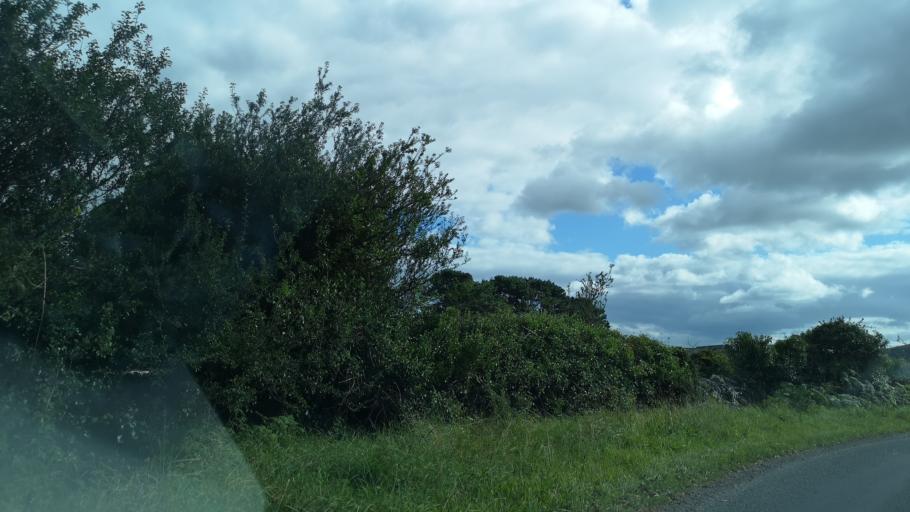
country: IE
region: Connaught
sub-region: County Galway
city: Moycullen
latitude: 53.3530
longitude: -9.1756
